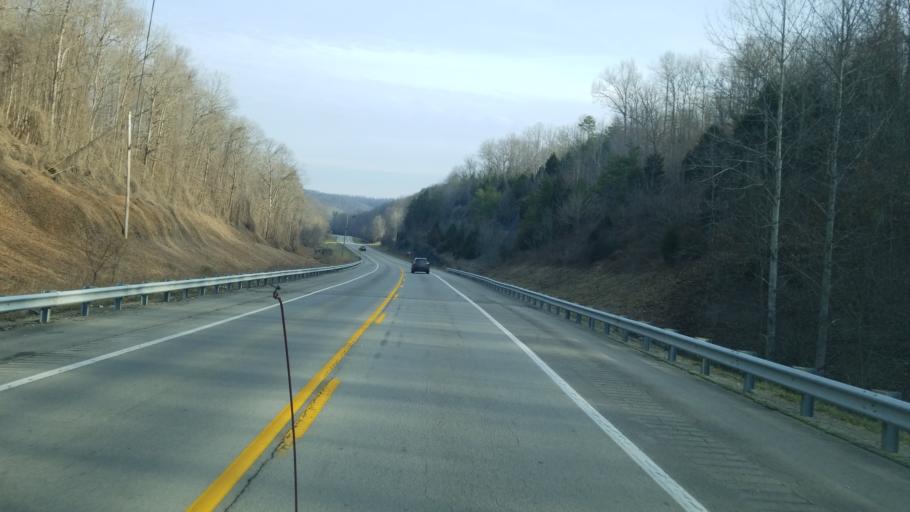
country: US
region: Kentucky
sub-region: Russell County
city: Russell Springs
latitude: 37.1476
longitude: -85.0271
